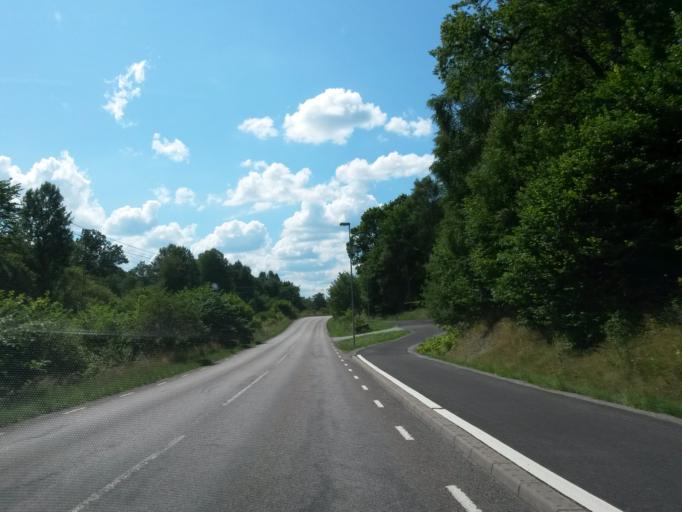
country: SE
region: Vaestra Goetaland
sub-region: Lerums Kommun
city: Stenkullen
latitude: 57.8051
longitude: 12.3500
